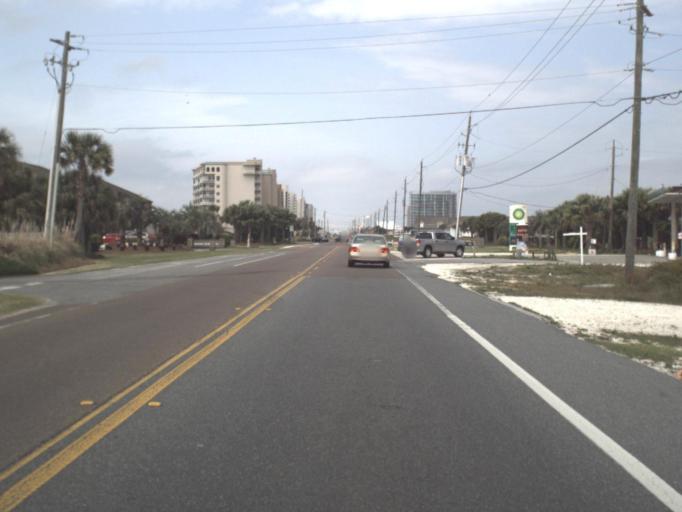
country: US
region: Alabama
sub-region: Baldwin County
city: Orange Beach
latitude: 30.2832
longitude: -87.5105
